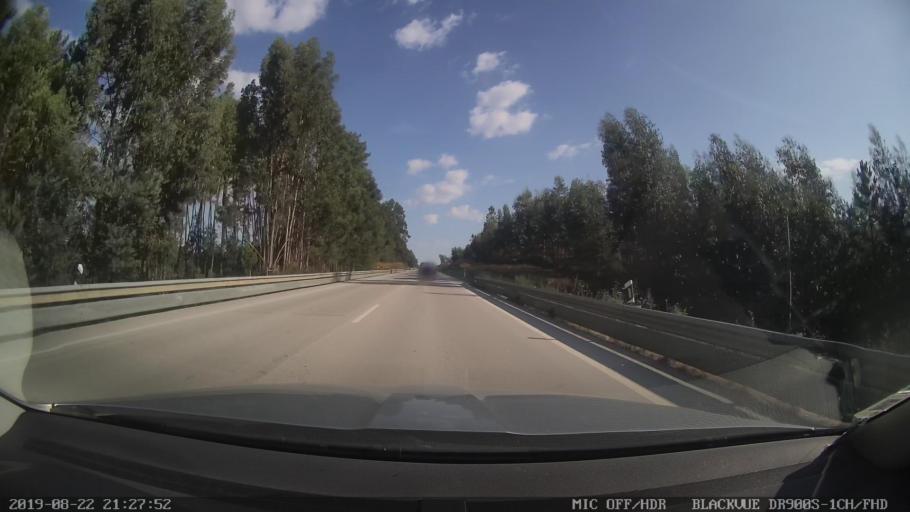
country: PT
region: Leiria
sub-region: Pedrogao Grande
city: Pedrogao Grande
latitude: 39.8847
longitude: -8.1203
